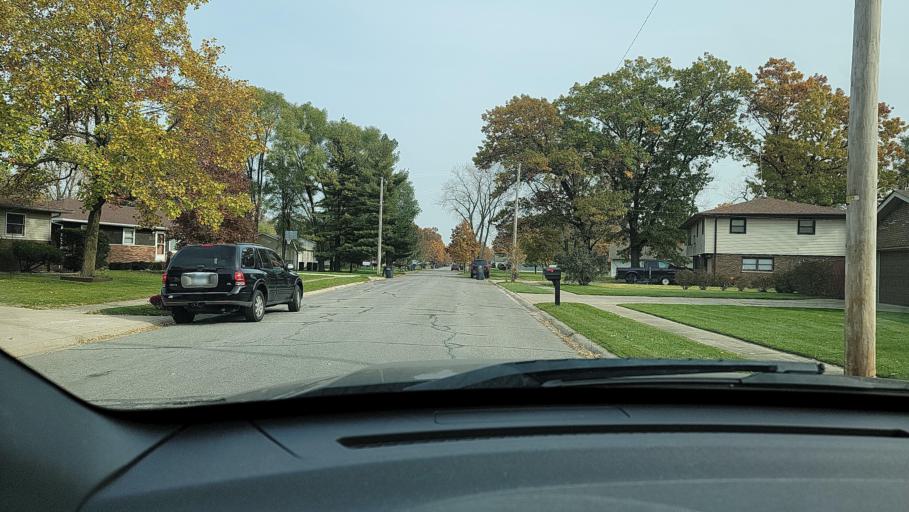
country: US
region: Indiana
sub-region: Porter County
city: Portage
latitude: 41.5899
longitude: -87.1706
